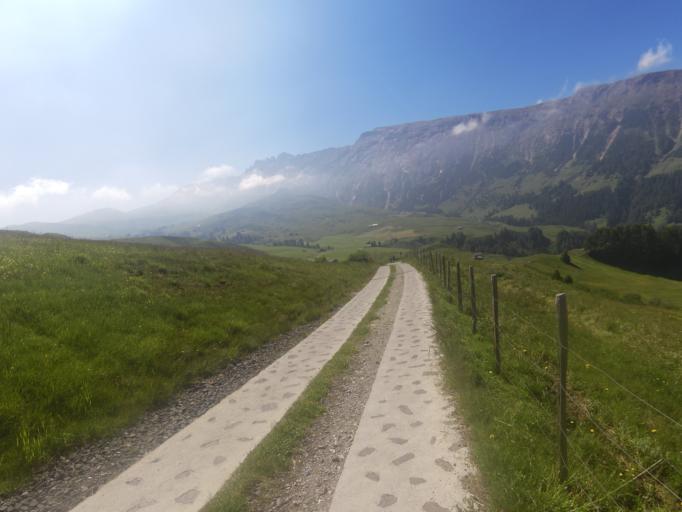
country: IT
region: Trentino-Alto Adige
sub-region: Bolzano
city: Siusi
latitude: 46.5253
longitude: 11.6061
